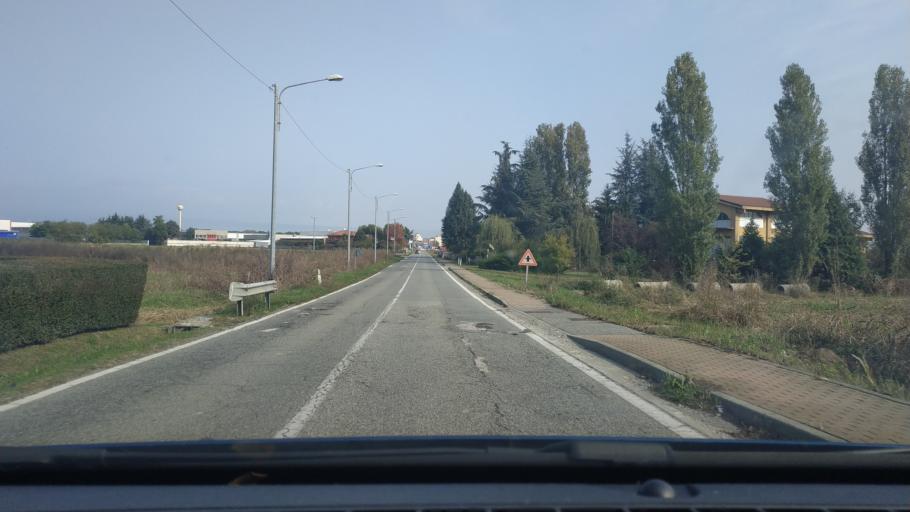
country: IT
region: Piedmont
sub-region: Provincia di Torino
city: Scarmagno
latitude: 45.3704
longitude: 7.8495
